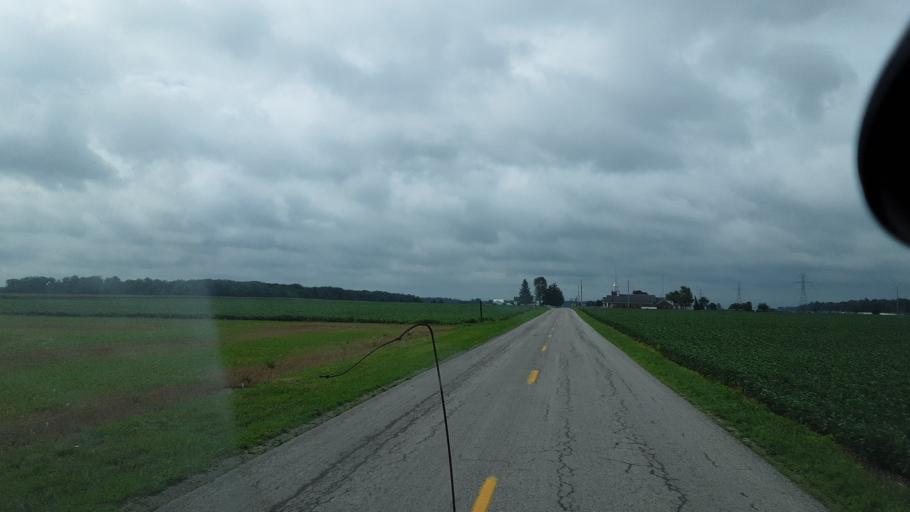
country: US
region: Indiana
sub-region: Allen County
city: Monroeville
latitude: 40.9729
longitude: -84.9692
